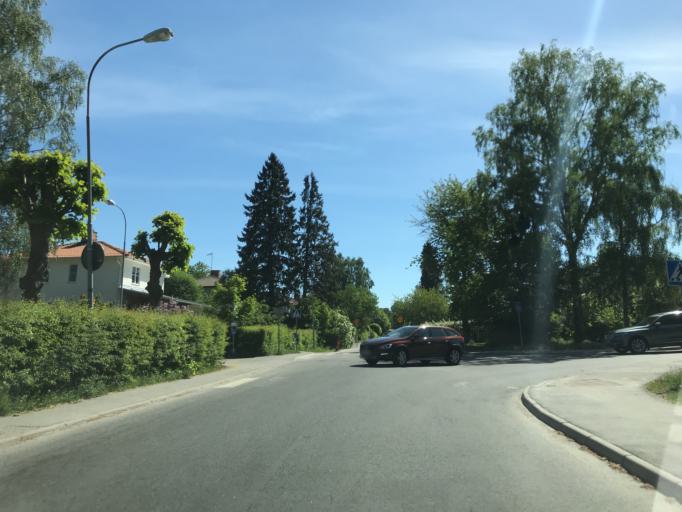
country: SE
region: Stockholm
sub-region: Sollentuna Kommun
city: Sollentuna
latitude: 59.4255
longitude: 17.9564
